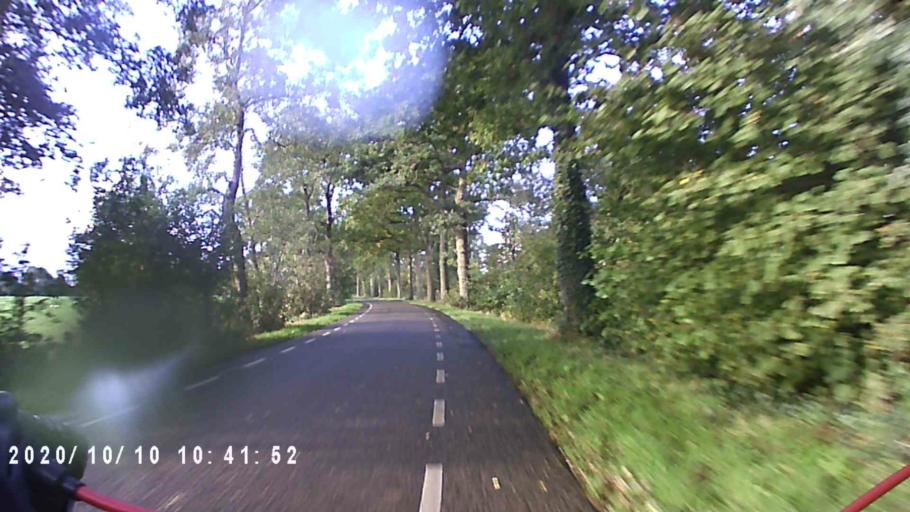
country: NL
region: Groningen
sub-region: Gemeente Grootegast
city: Grootegast
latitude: 53.1756
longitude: 6.2760
